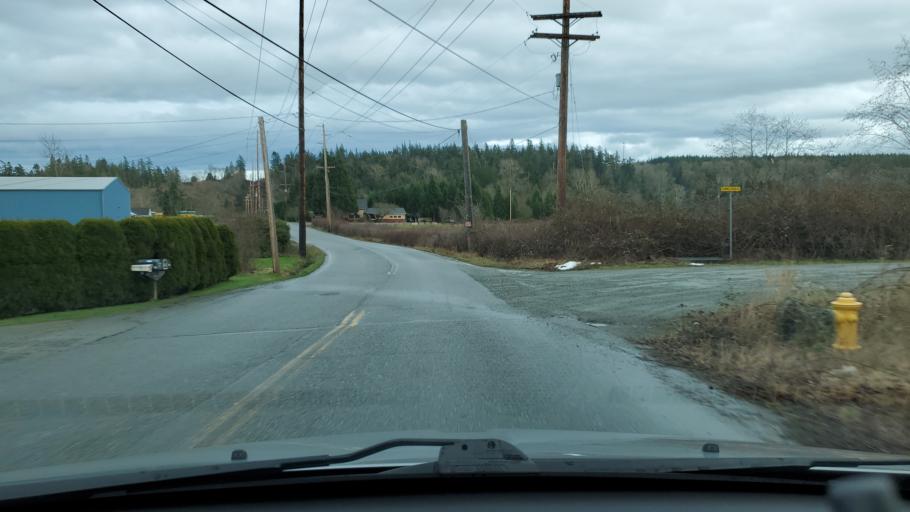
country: US
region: Washington
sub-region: Skagit County
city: Anacortes
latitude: 48.4584
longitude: -122.5522
